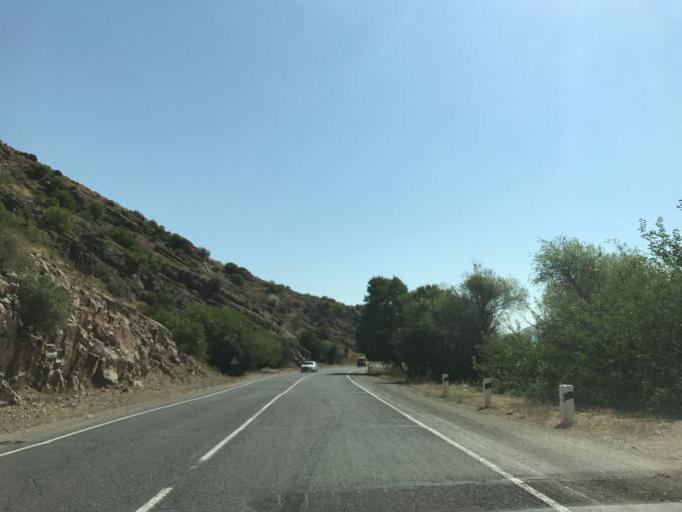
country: AM
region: Vayots' Dzori Marz
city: Aghavnadzor
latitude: 39.7345
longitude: 45.2362
